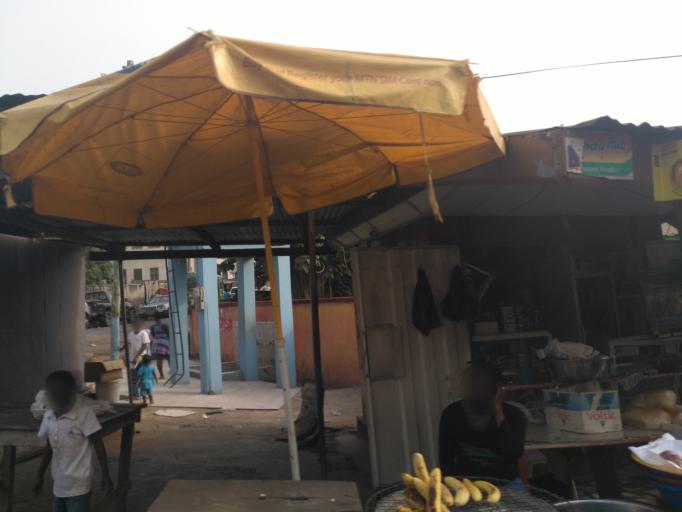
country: GH
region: Ashanti
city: Kumasi
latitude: 6.6868
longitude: -1.6135
